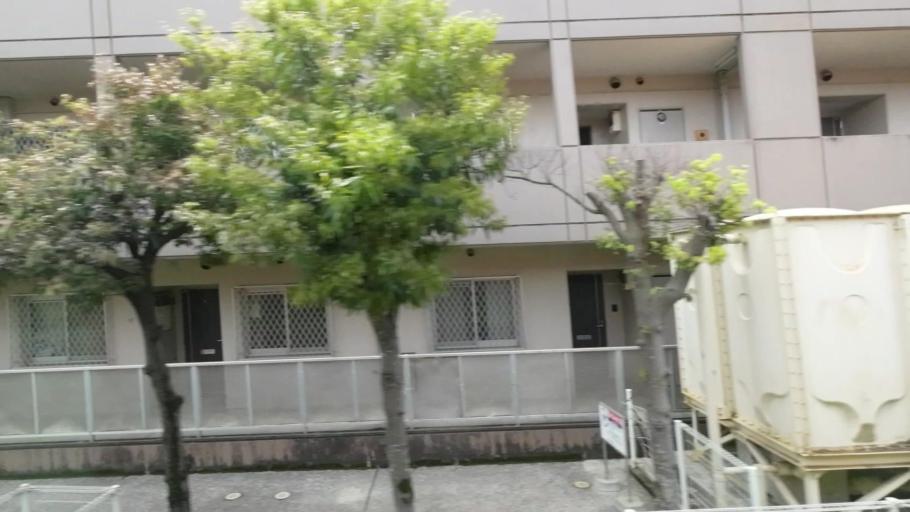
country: JP
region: Kochi
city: Kochi-shi
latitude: 33.5783
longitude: 133.6377
